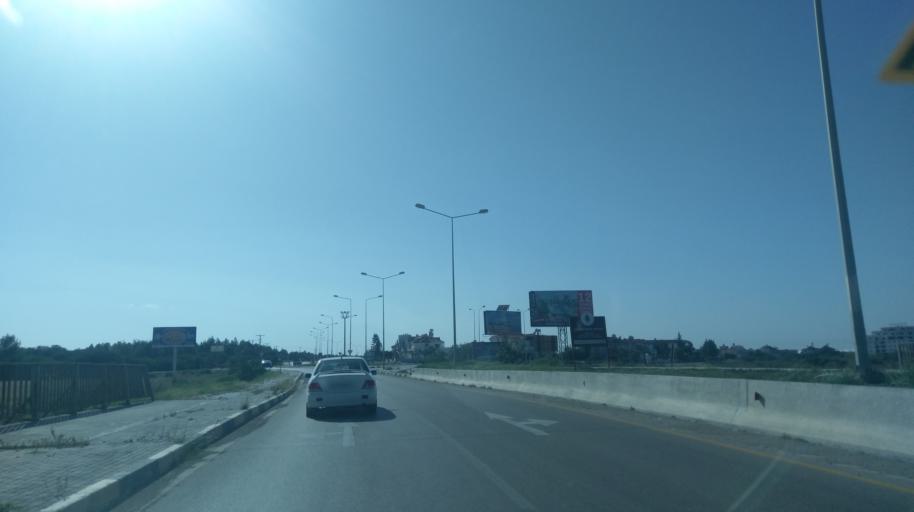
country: CY
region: Ammochostos
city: Trikomo
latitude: 35.2484
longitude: 33.9011
